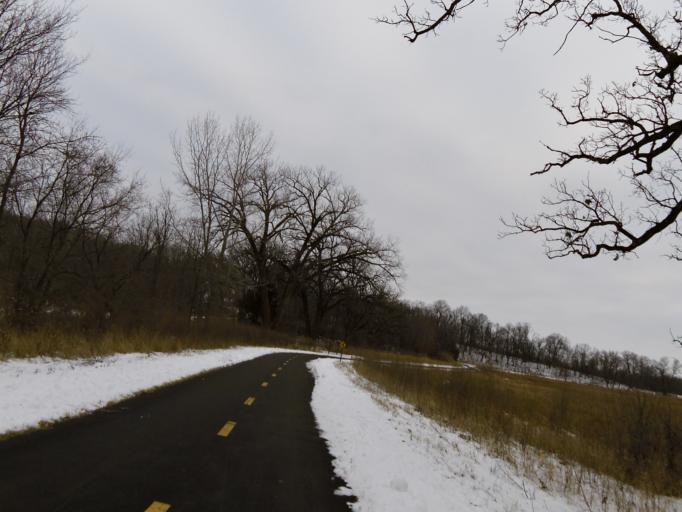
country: US
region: Minnesota
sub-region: Scott County
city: Prior Lake
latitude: 44.7118
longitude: -93.4672
